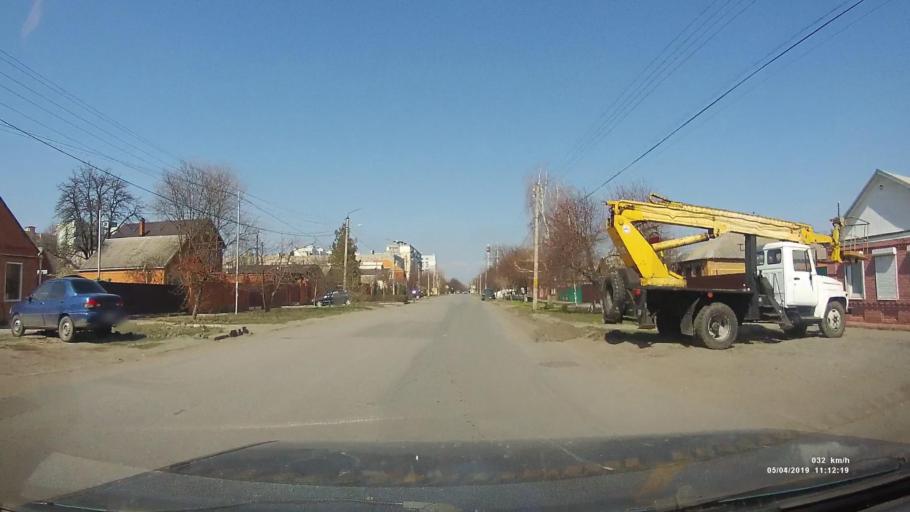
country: RU
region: Rostov
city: Azov
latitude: 47.0975
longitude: 39.4380
